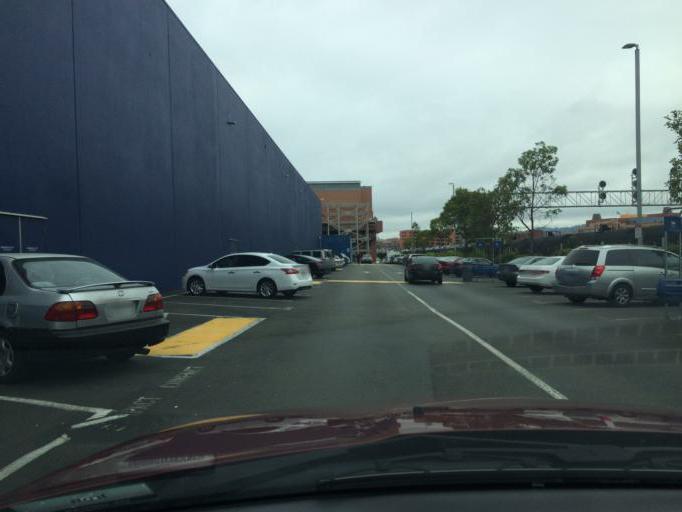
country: US
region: California
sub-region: Alameda County
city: Emeryville
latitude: 37.8312
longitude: -122.2913
